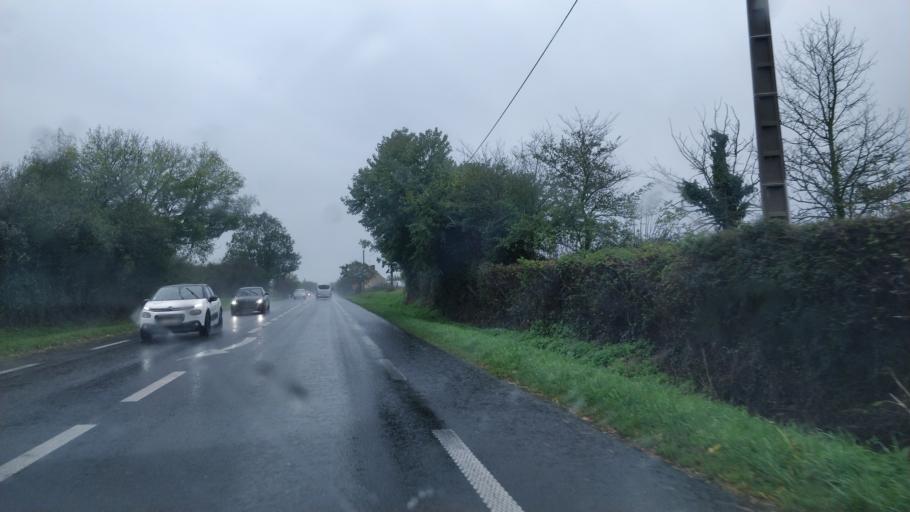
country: FR
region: Lower Normandy
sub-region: Departement de la Manche
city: Brehal
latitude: 48.8797
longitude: -1.5316
